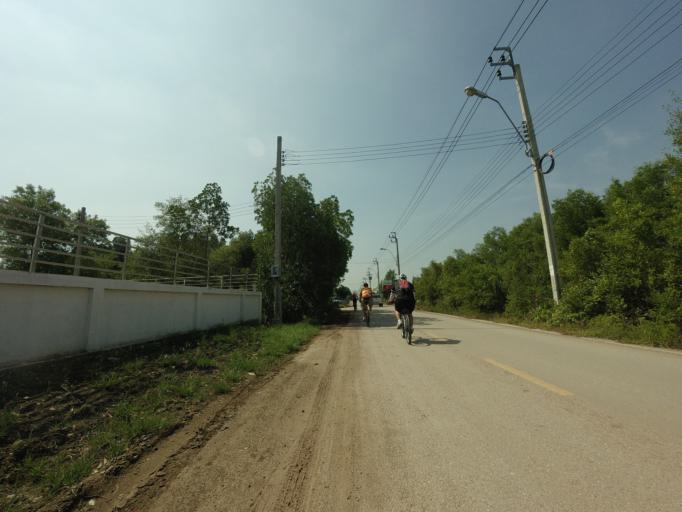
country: TH
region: Bangkok
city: Thung Khru
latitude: 13.5401
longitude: 100.4434
